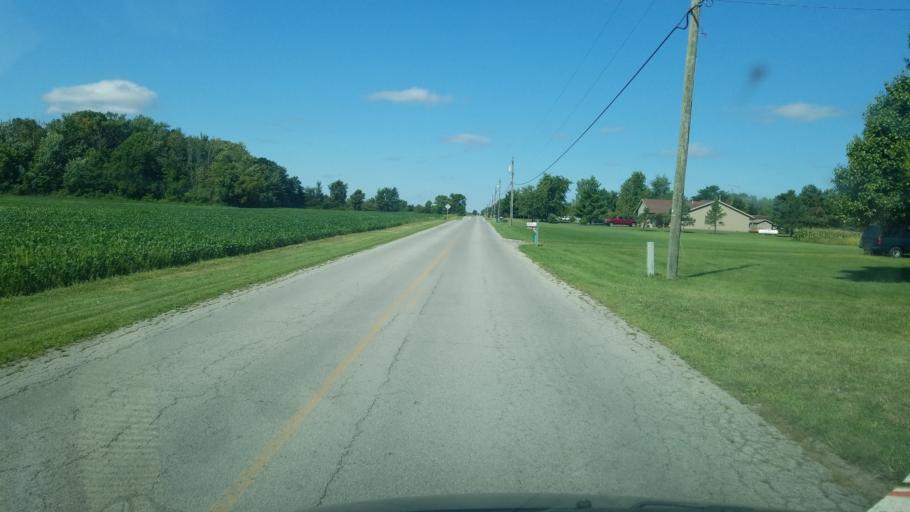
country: US
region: Ohio
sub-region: Hancock County
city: Findlay
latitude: 41.1092
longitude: -83.5975
